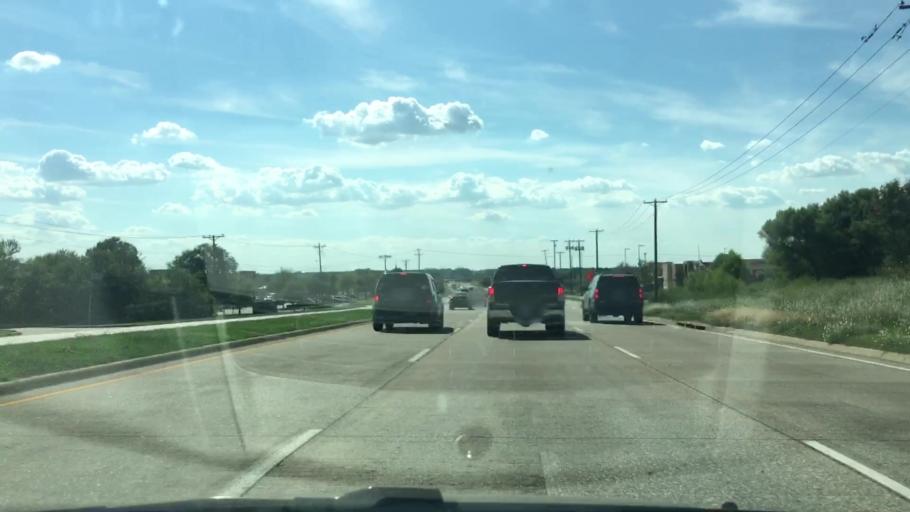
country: US
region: Texas
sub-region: Collin County
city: McKinney
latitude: 33.2182
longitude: -96.6759
